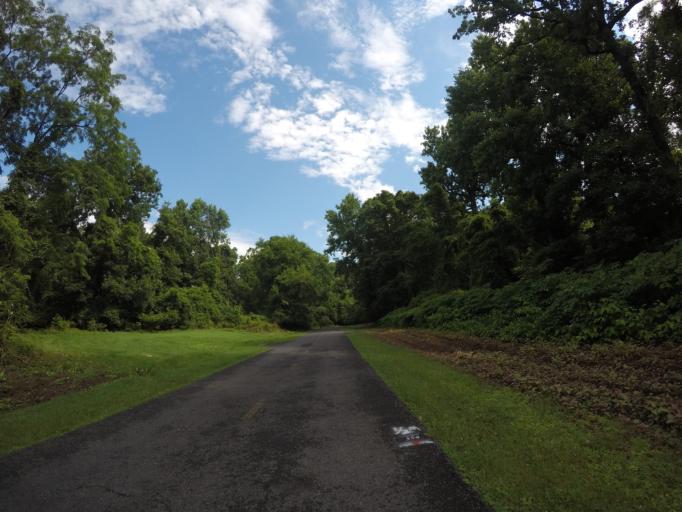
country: US
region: Maryland
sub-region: Prince George's County
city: East Riverdale
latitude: 38.9690
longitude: -76.9214
